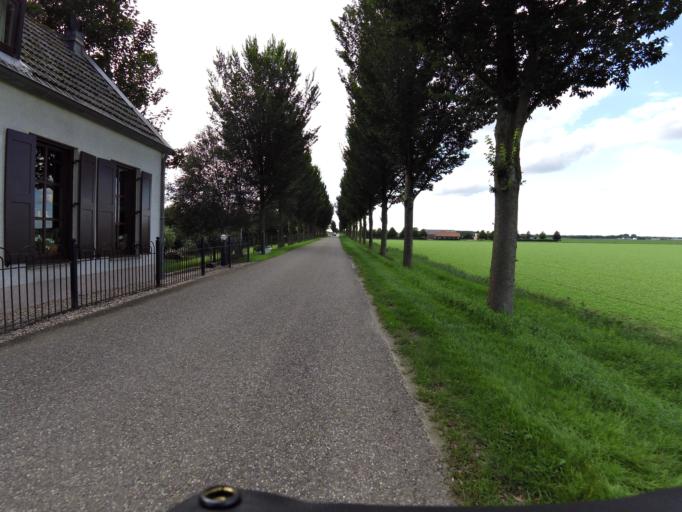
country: NL
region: North Brabant
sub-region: Gemeente Steenbergen
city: Nieuw-Vossemeer
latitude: 51.6758
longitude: 4.2433
